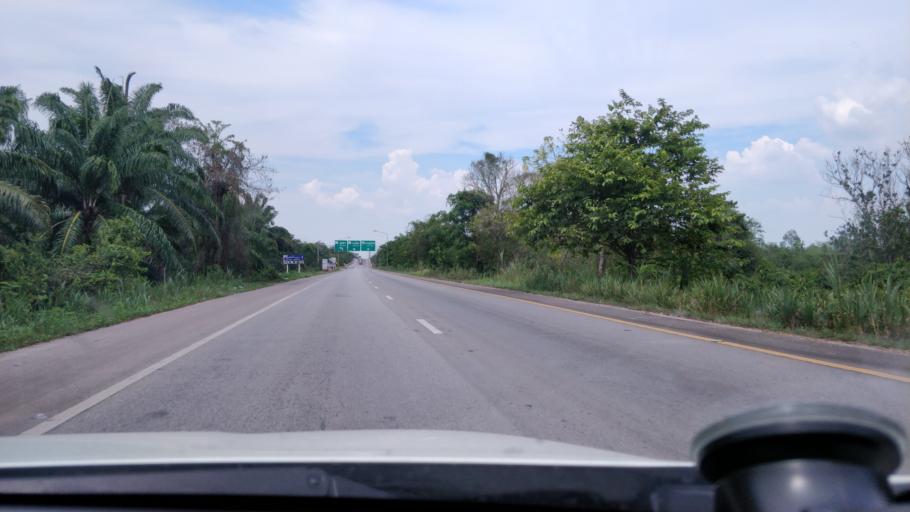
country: TH
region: Surat Thani
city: Ban Na Doem
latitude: 8.9317
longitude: 99.2614
